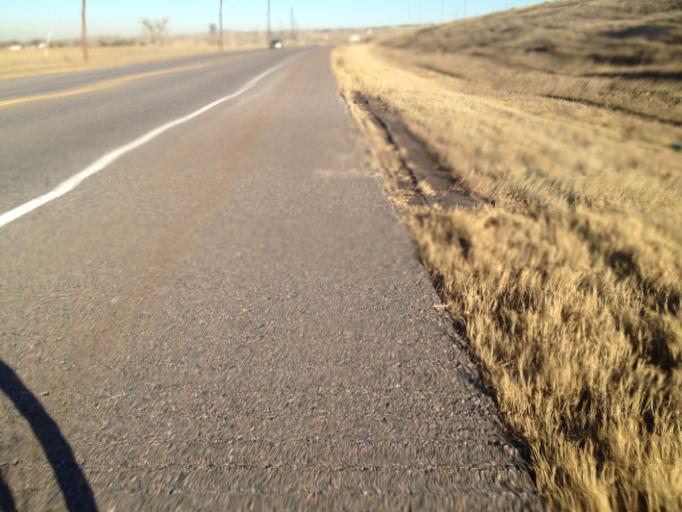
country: US
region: Colorado
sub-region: Boulder County
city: Louisville
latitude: 39.9584
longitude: -105.1036
